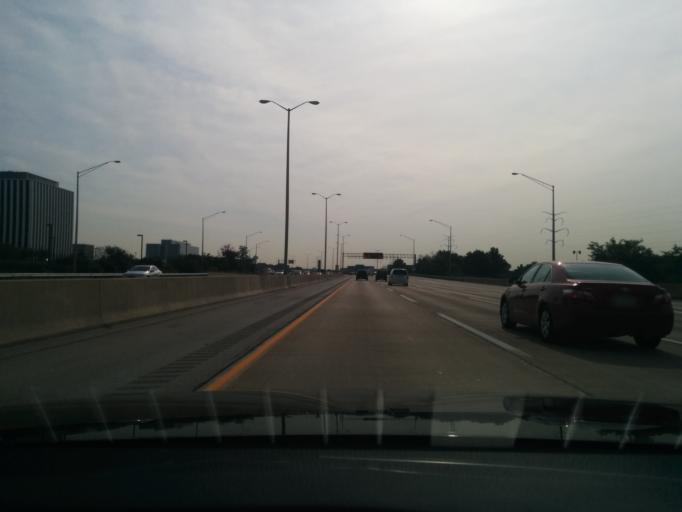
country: US
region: Illinois
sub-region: DuPage County
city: Oakbrook Terrace
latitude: 41.8446
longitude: -87.9528
